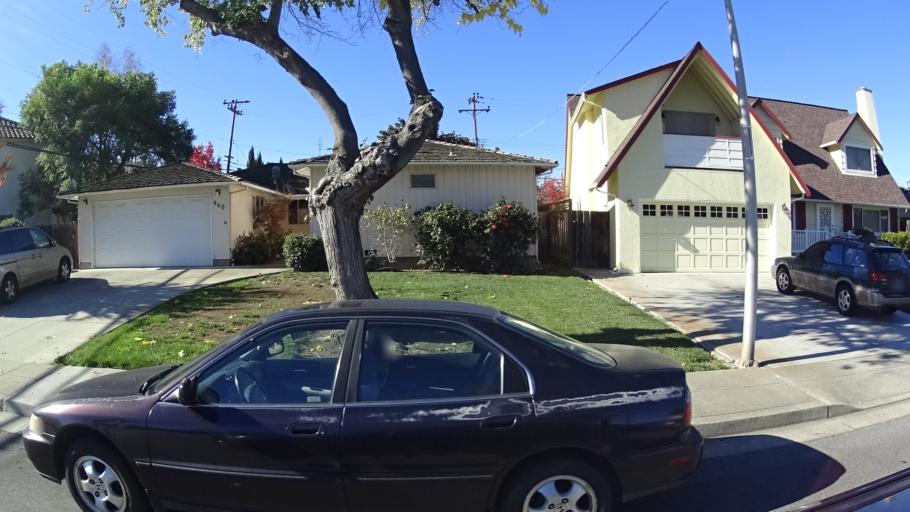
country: US
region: California
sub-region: Santa Clara County
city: Cupertino
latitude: 37.3433
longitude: -121.9987
